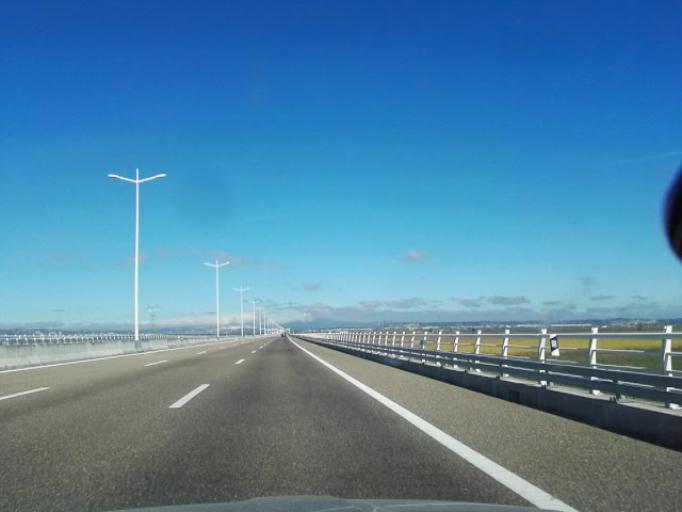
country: PT
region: Santarem
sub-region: Benavente
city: Samora Correia
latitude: 38.9771
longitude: -8.8811
